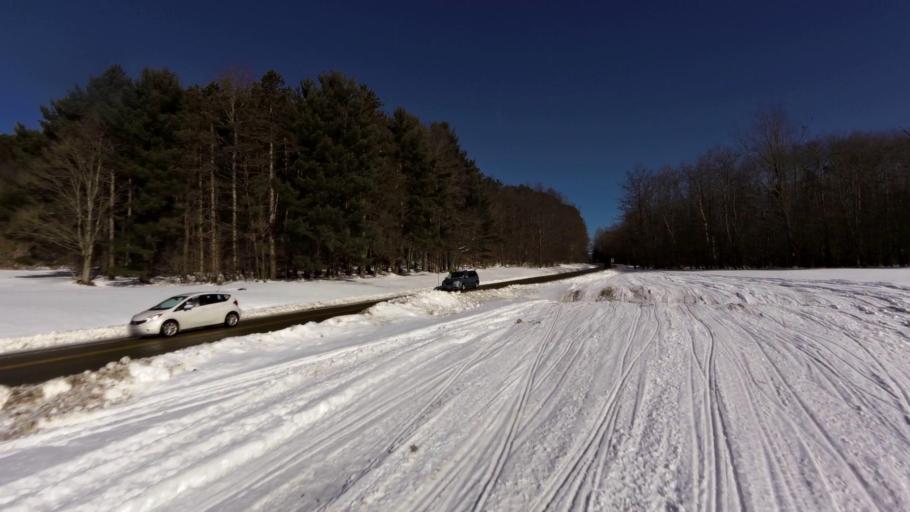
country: US
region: New York
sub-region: Cattaraugus County
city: Salamanca
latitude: 42.1091
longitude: -78.7455
